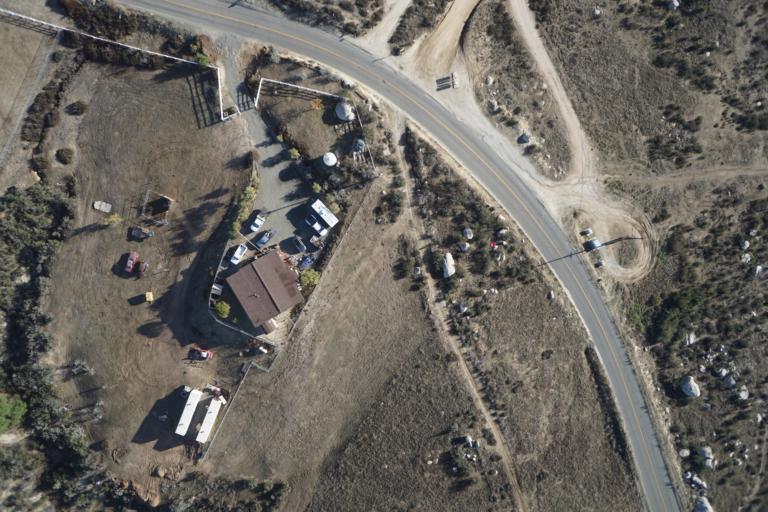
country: US
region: California
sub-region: Riverside County
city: East Hemet
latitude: 33.6196
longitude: -116.9006
